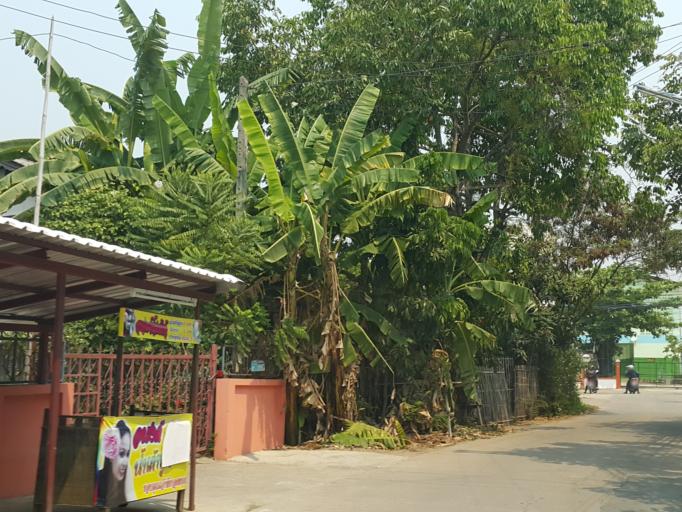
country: TH
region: Chiang Mai
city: Hang Dong
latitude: 18.7244
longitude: 98.9563
